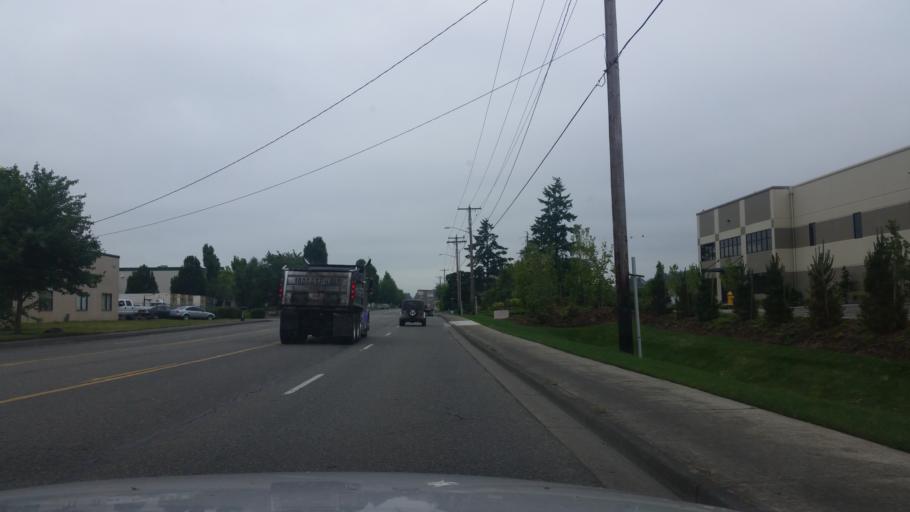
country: US
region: Washington
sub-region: Pierce County
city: Sumner
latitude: 47.2270
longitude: -122.2400
